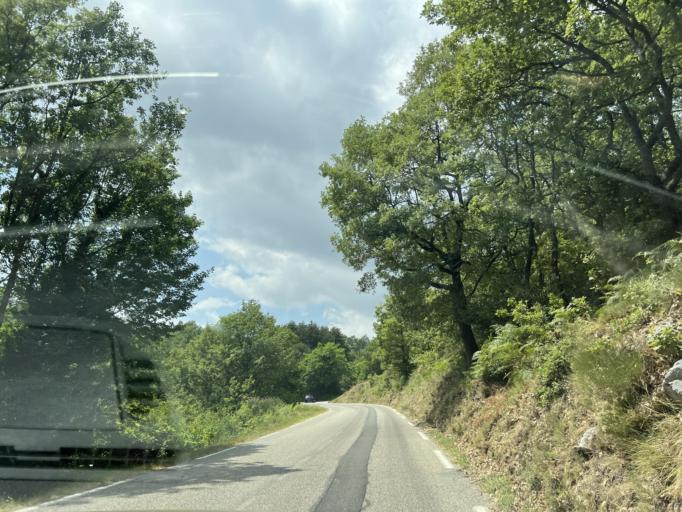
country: FR
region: Provence-Alpes-Cote d'Azur
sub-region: Departement des Alpes-Maritimes
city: Tourrettes-sur-Loup
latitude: 43.7961
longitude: 6.9536
